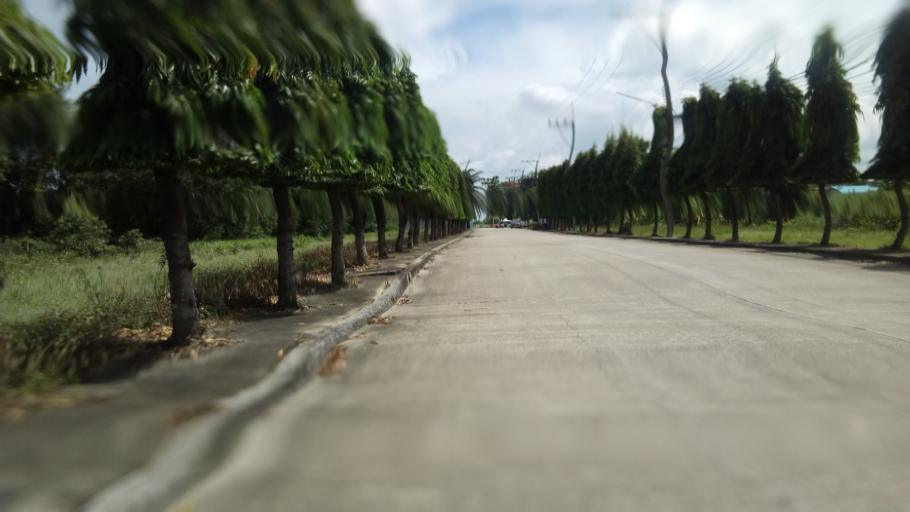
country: TH
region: Pathum Thani
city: Nong Suea
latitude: 14.0629
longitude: 100.8605
